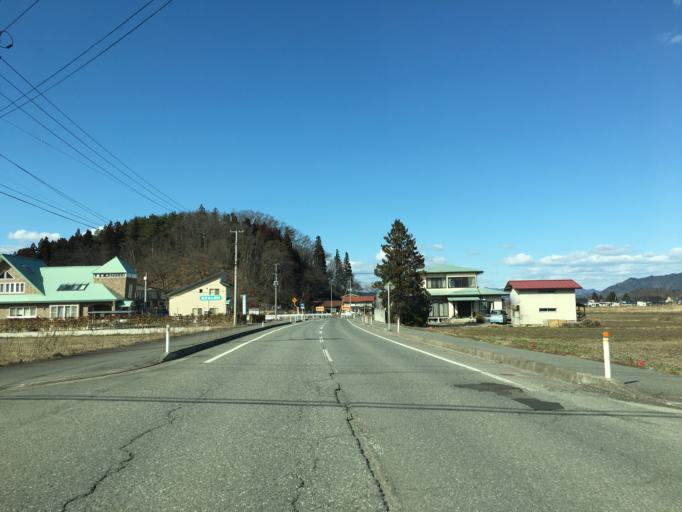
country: JP
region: Yamagata
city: Yonezawa
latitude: 37.9230
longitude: 140.1461
